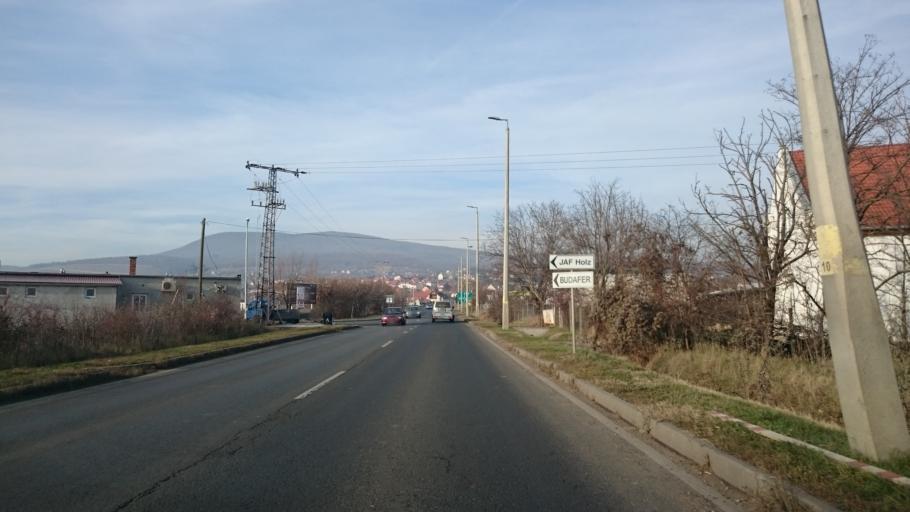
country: HU
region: Baranya
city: Pellerd
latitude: 46.0626
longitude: 18.1745
